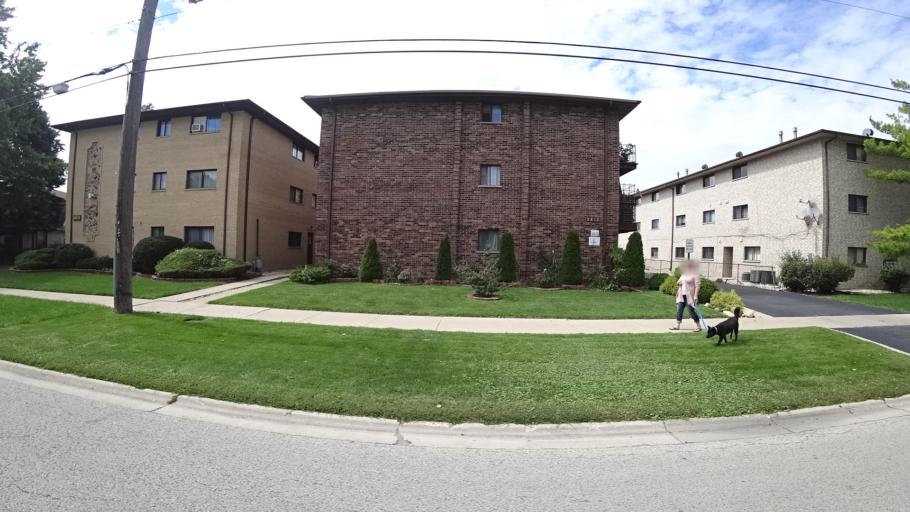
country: US
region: Illinois
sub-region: Cook County
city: Chicago Ridge
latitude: 41.7134
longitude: -87.7939
